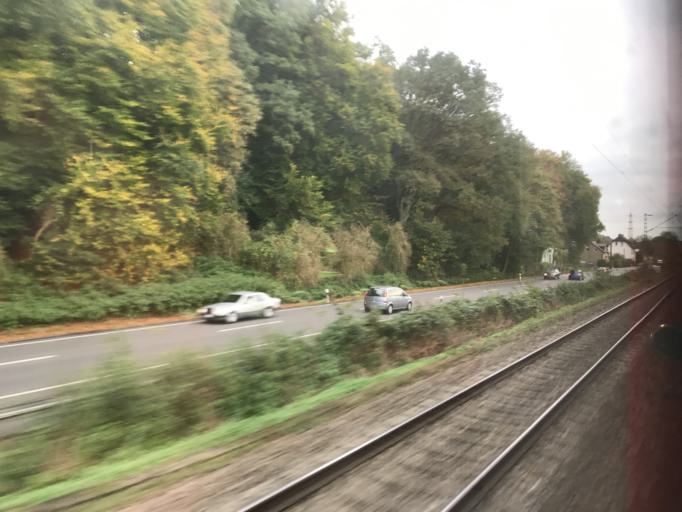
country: DE
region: North Rhine-Westphalia
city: Witten
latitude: 51.4183
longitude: 7.3538
